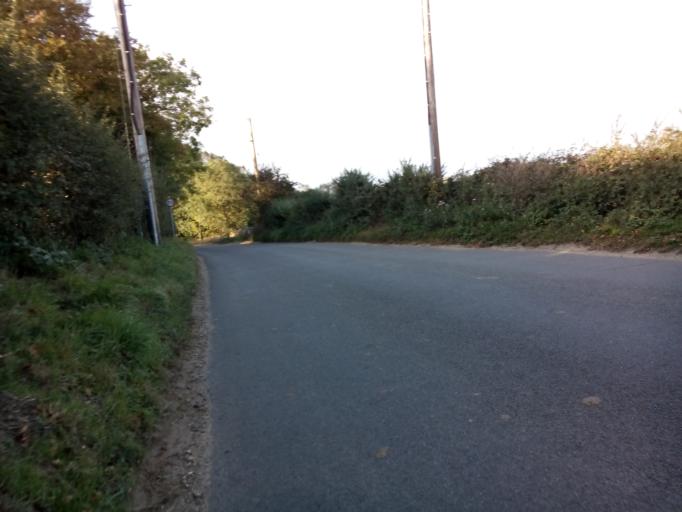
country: GB
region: England
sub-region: Suffolk
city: Bramford
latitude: 52.0297
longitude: 1.0929
